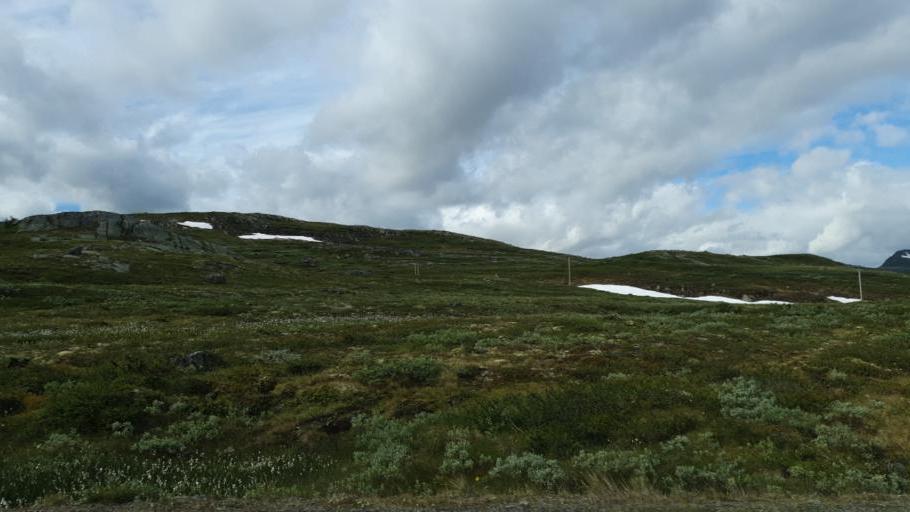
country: NO
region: Oppland
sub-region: Vestre Slidre
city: Slidre
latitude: 61.3261
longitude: 8.8020
